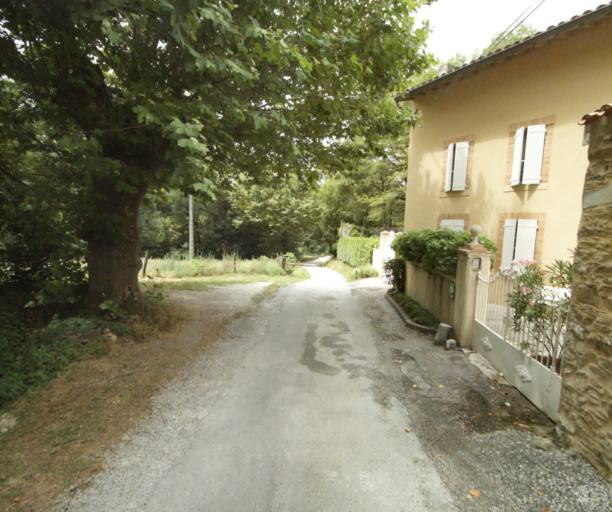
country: FR
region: Midi-Pyrenees
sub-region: Departement du Tarn
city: Soreze
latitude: 43.4504
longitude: 2.0717
